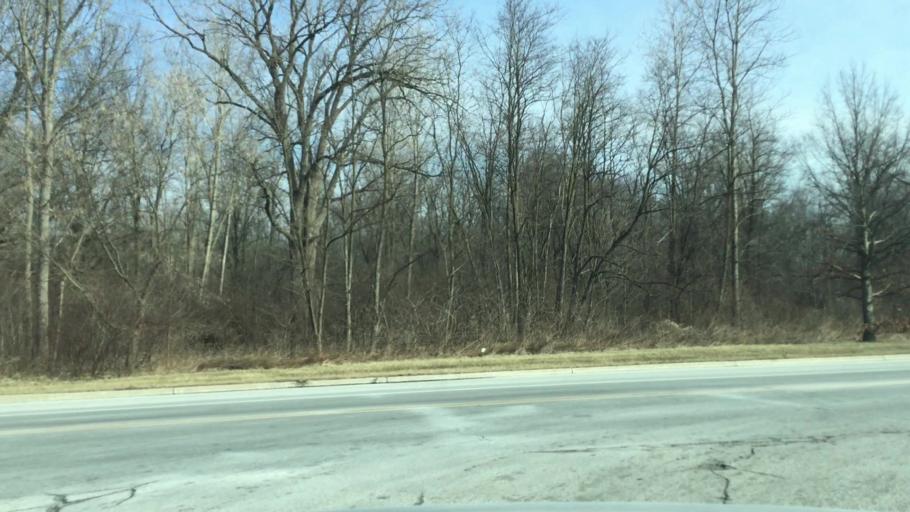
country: US
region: Michigan
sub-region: Wayne County
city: Flat Rock
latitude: 42.1380
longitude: -83.2900
